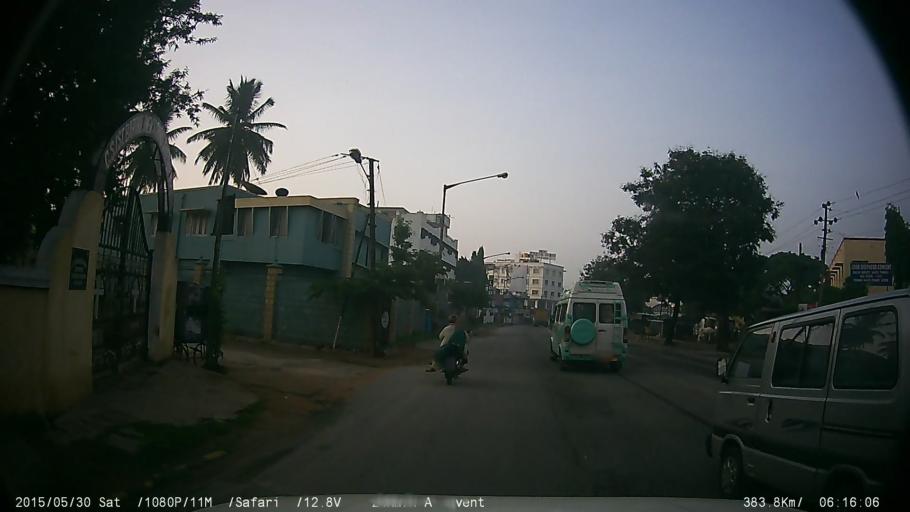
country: IN
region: Karnataka
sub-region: Mysore
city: Mysore
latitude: 12.3206
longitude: 76.6614
